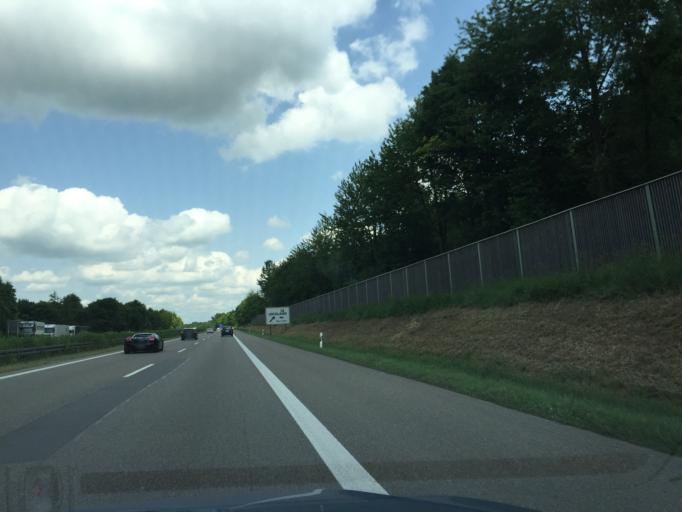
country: DE
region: Bavaria
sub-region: Swabia
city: Nersingen
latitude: 48.4336
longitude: 10.1051
